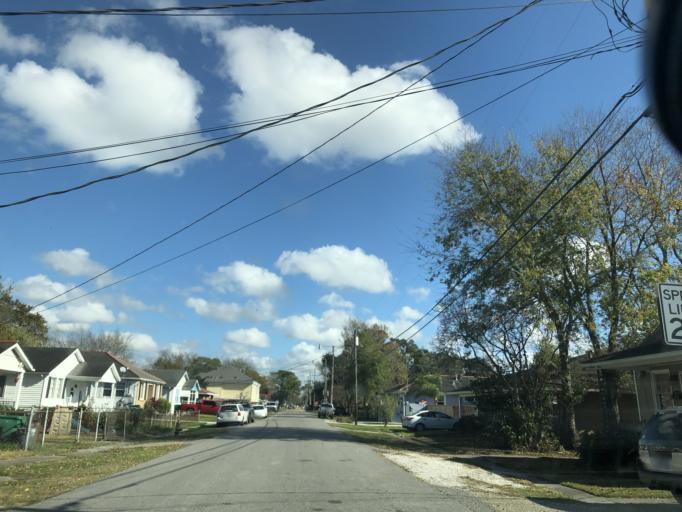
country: US
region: Louisiana
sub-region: Jefferson Parish
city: Metairie Terrace
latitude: 29.9785
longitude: -90.1687
